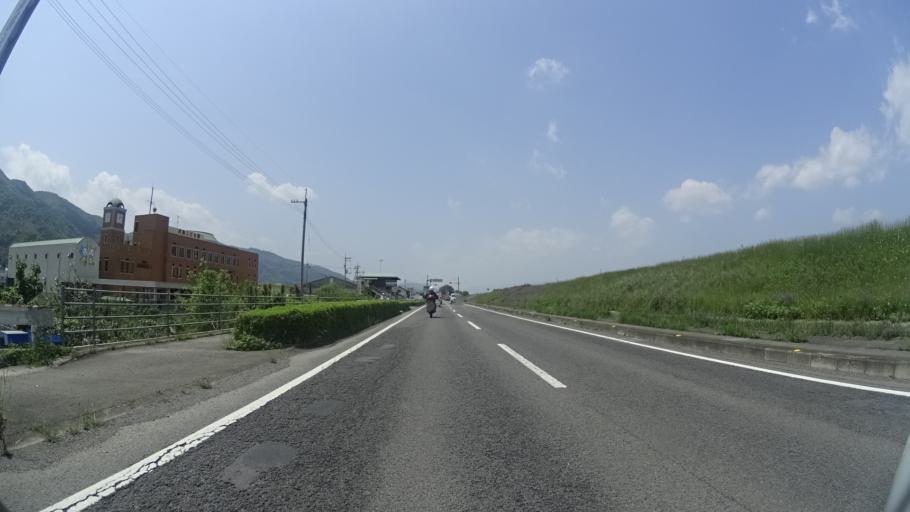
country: JP
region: Tokushima
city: Kamojimacho-jogejima
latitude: 34.0606
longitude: 134.3054
